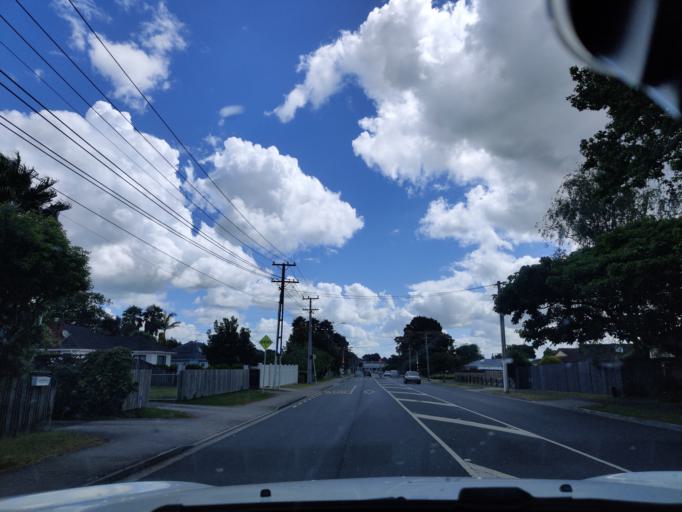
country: NZ
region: Auckland
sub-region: Auckland
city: Papakura
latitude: -37.0601
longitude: 174.9512
